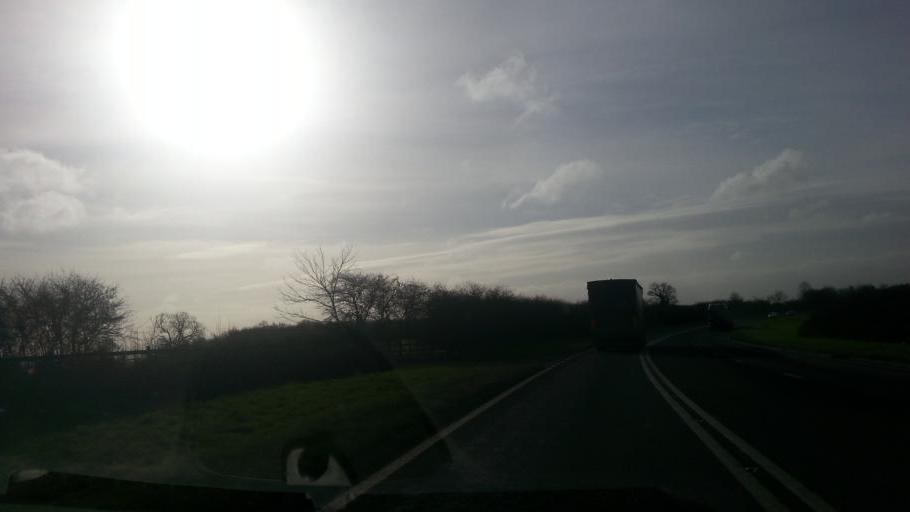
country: GB
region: England
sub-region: District of Rutland
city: Ridlington
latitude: 52.5974
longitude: -0.7585
